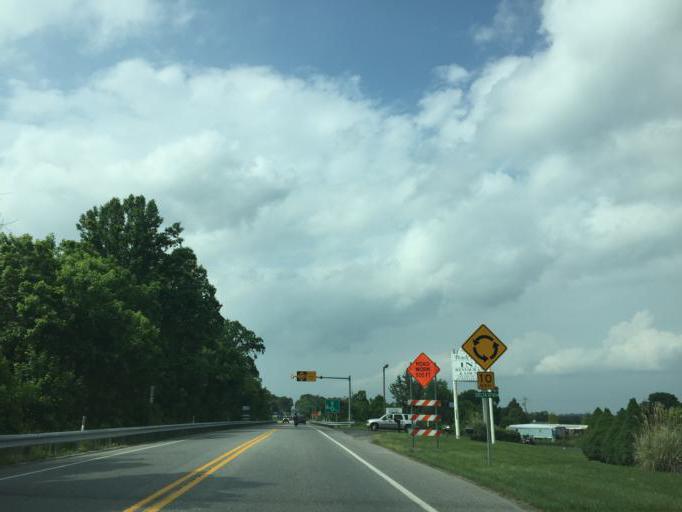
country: US
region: Pennsylvania
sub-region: York County
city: Susquehanna Trails
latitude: 39.7438
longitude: -76.3318
